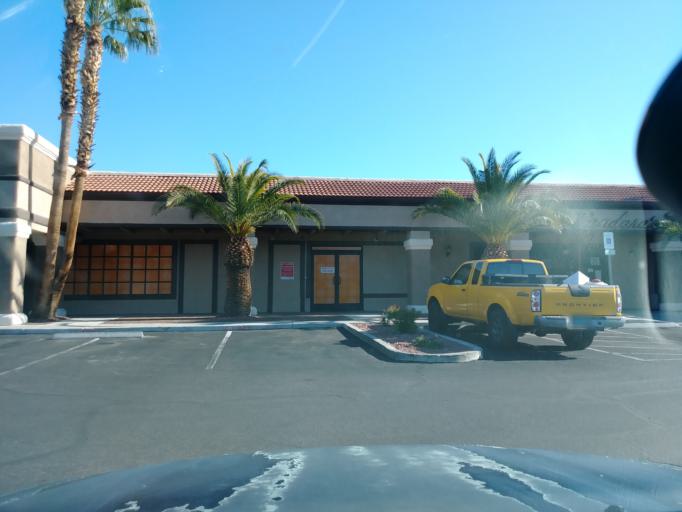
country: US
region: Nevada
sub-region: Clark County
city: Spring Valley
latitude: 36.1795
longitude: -115.2416
